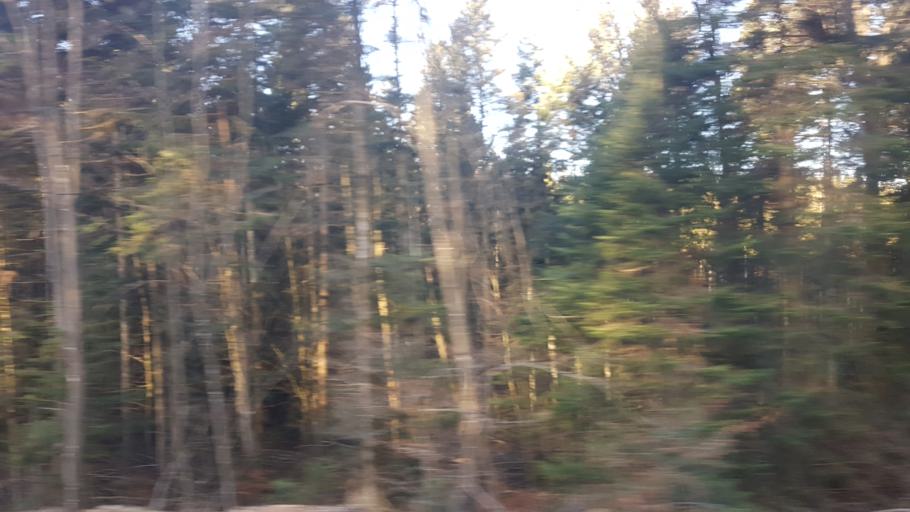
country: FR
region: Lorraine
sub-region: Departement des Vosges
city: Xertigny
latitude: 48.0745
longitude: 6.4197
